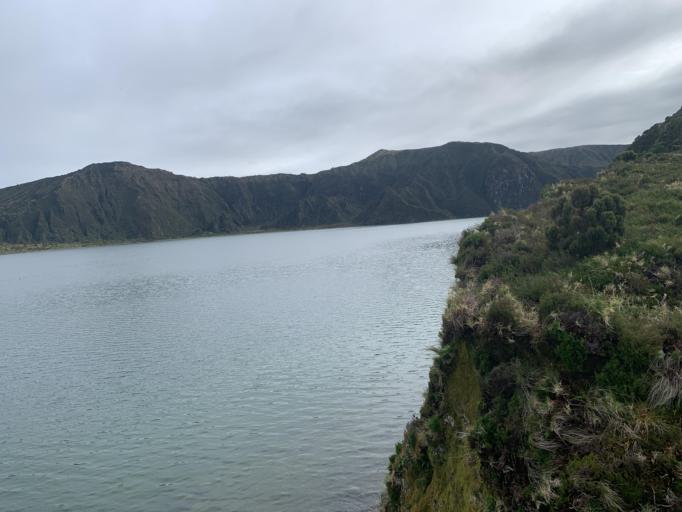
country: PT
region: Azores
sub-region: Vila Franca do Campo
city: Vila Franca do Campo
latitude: 37.7605
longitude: -25.4804
